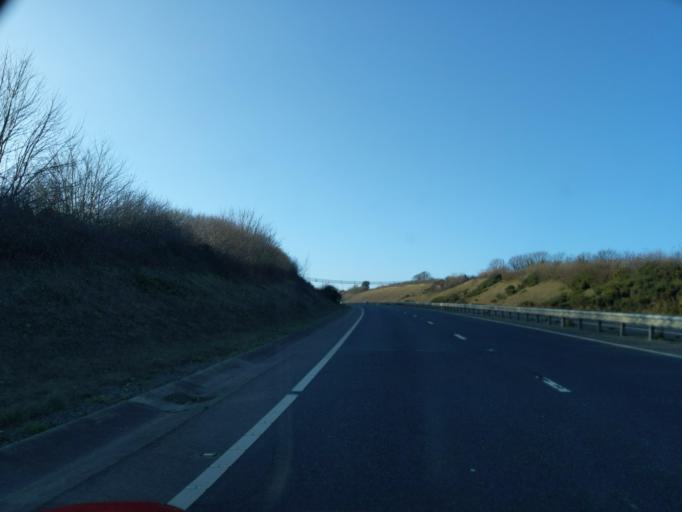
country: GB
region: England
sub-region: Cornwall
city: Liskeard
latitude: 50.4599
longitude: -4.5125
